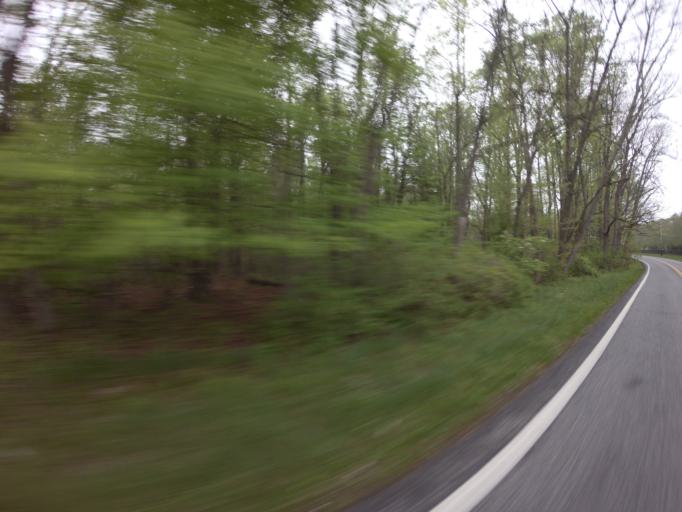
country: US
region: Maryland
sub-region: Baltimore County
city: Reisterstown
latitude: 39.4785
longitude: -76.8003
